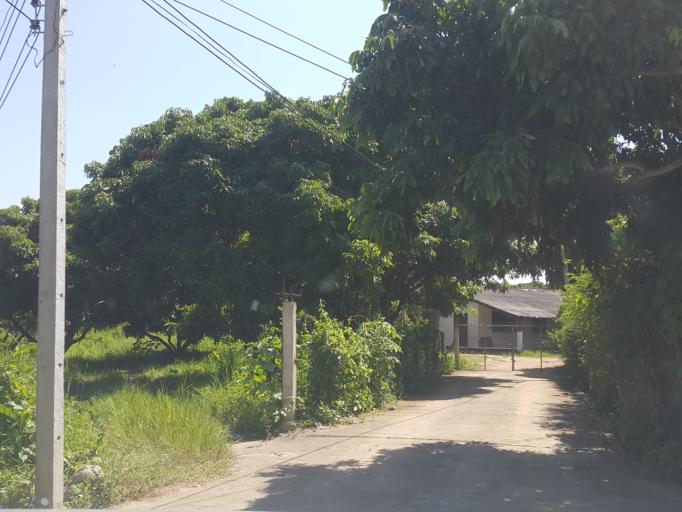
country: TH
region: Chiang Mai
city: Saraphi
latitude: 18.7619
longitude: 99.0564
